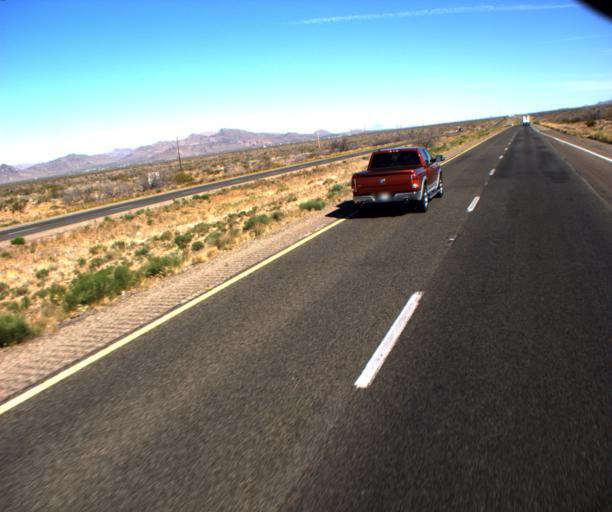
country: US
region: Arizona
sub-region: Mohave County
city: Golden Valley
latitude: 35.3003
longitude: -114.1892
